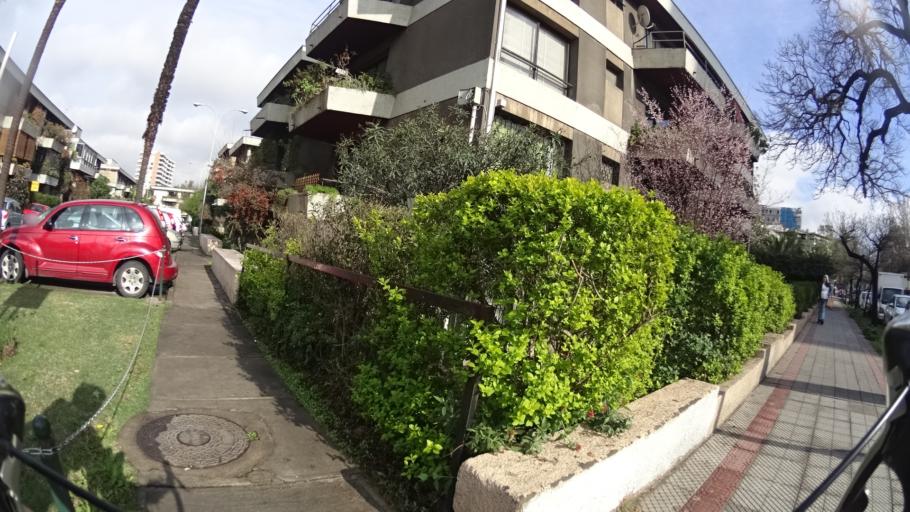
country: CL
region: Santiago Metropolitan
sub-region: Provincia de Santiago
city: Santiago
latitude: -33.4340
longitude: -70.6172
